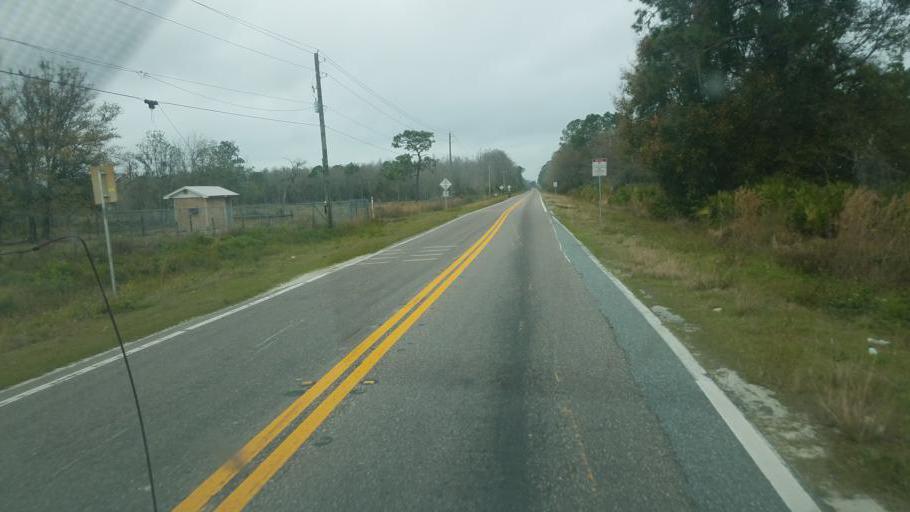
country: US
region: Florida
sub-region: Polk County
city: Polk City
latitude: 28.2585
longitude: -81.8262
